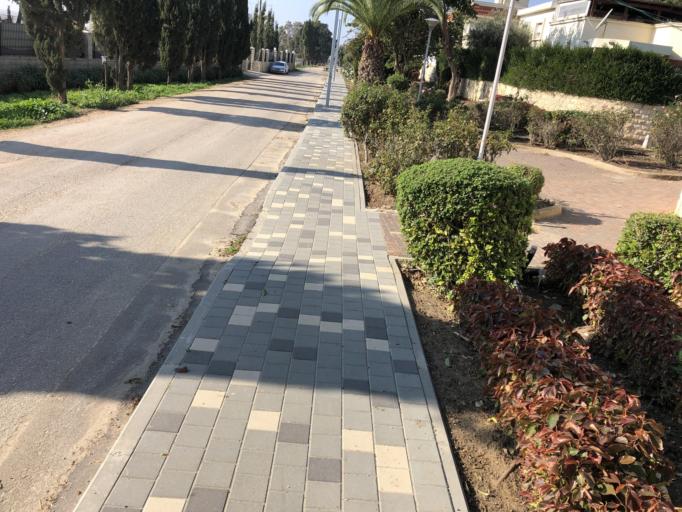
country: IL
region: Northern District
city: `Akko
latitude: 32.9179
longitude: 35.0902
